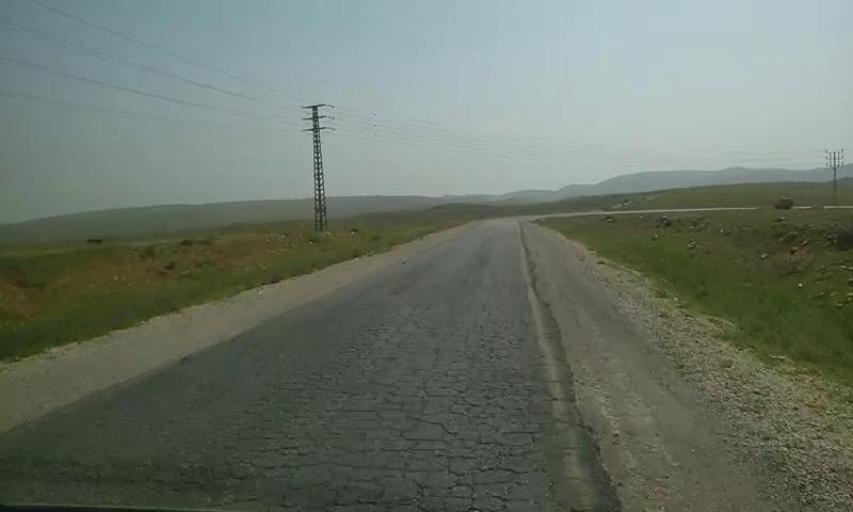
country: PS
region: West Bank
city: An Nuway`imah
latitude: 31.9212
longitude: 35.4173
